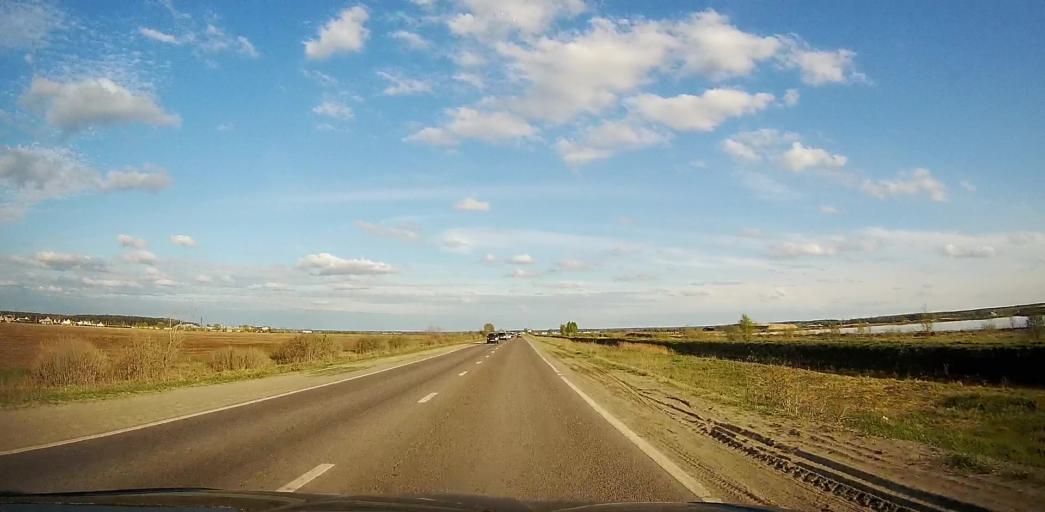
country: RU
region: Moskovskaya
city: Malyshevo
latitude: 55.5109
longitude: 38.2812
